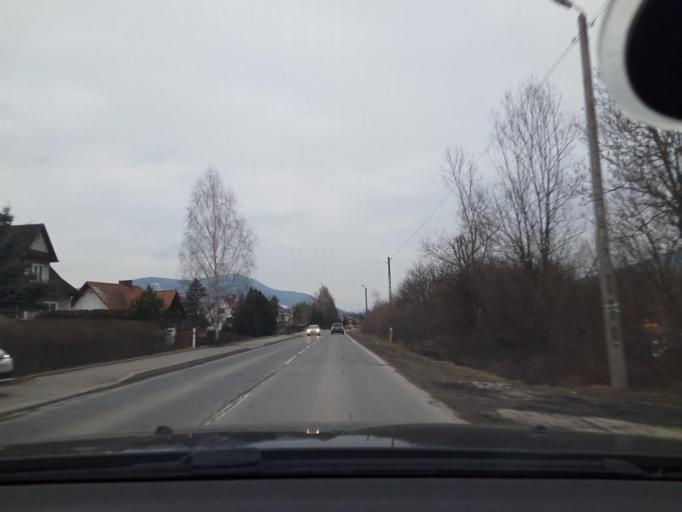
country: PL
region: Lesser Poland Voivodeship
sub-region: Powiat limanowski
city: Mszana Gorna
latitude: 49.6634
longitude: 20.0928
